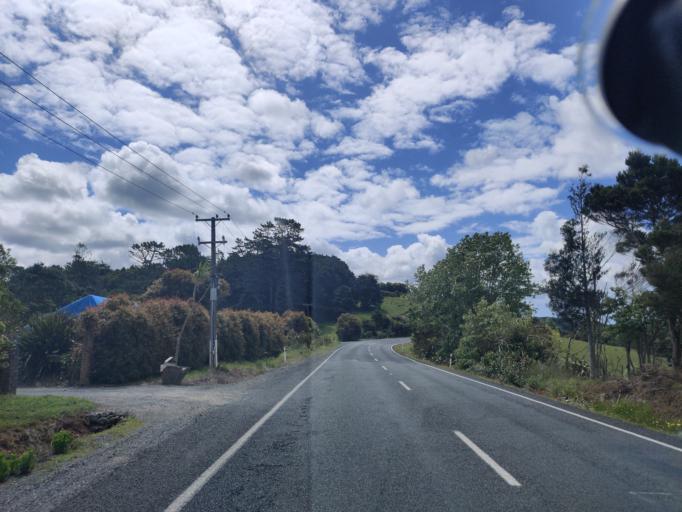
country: NZ
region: Northland
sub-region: Far North District
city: Kerikeri
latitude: -35.1498
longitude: 173.8845
